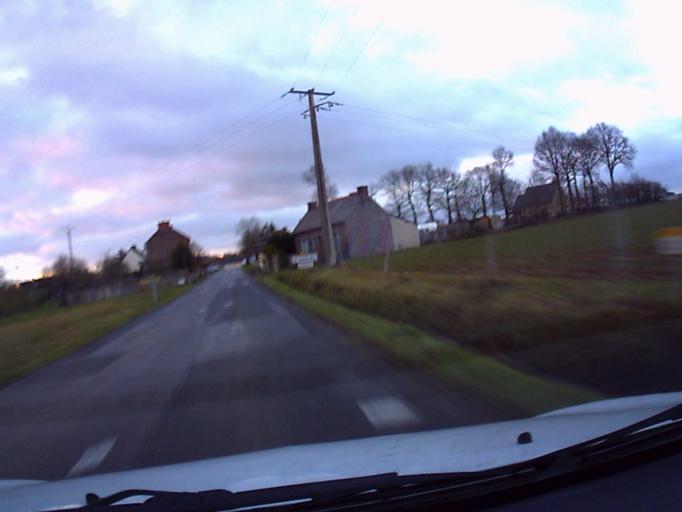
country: FR
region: Brittany
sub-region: Departement d'Ille-et-Vilaine
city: Iffendic
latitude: 48.1122
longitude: -2.0626
